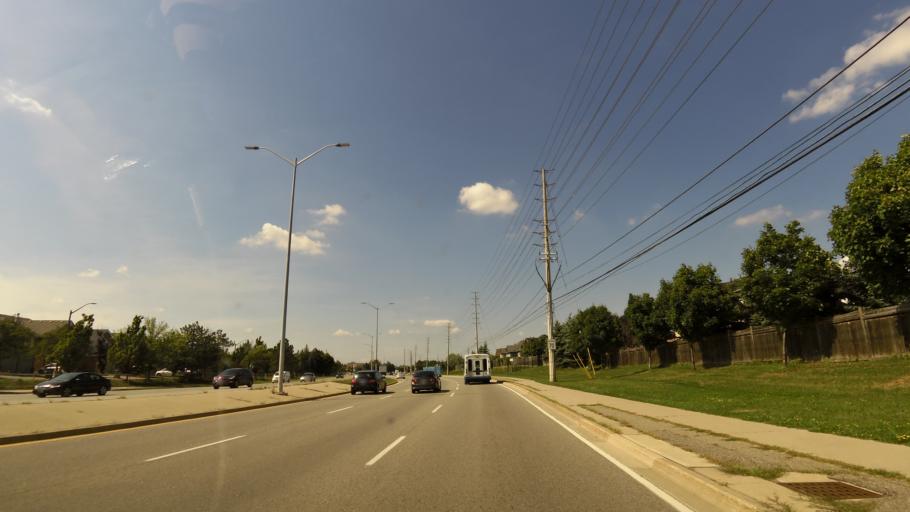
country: CA
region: Ontario
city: Mississauga
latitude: 43.5682
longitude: -79.7193
